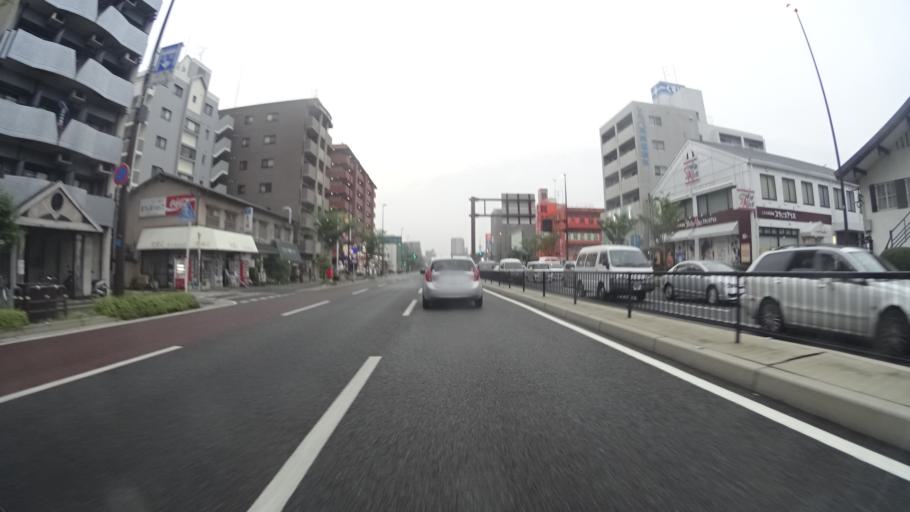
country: JP
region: Fukuoka
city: Fukuoka-shi
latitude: 33.5640
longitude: 130.4230
